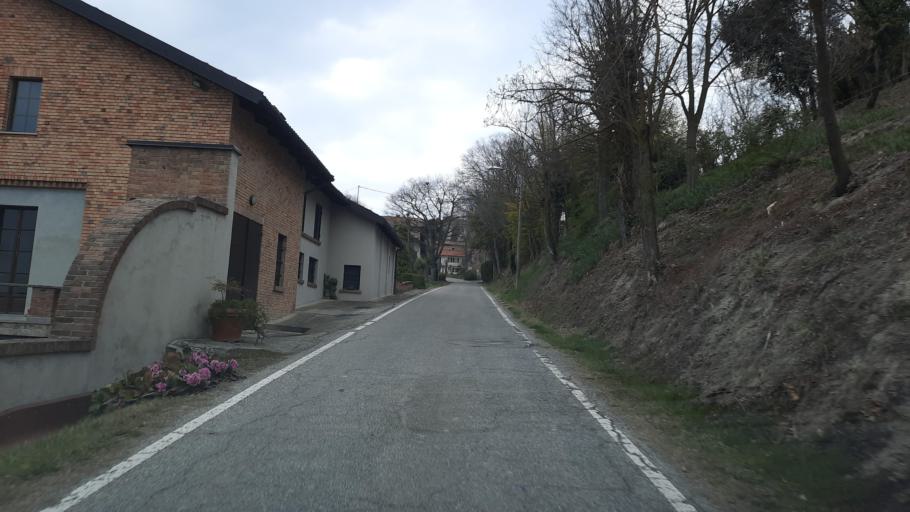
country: IT
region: Piedmont
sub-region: Provincia di Alessandria
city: Odalengo Grande
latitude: 45.1074
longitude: 8.1696
